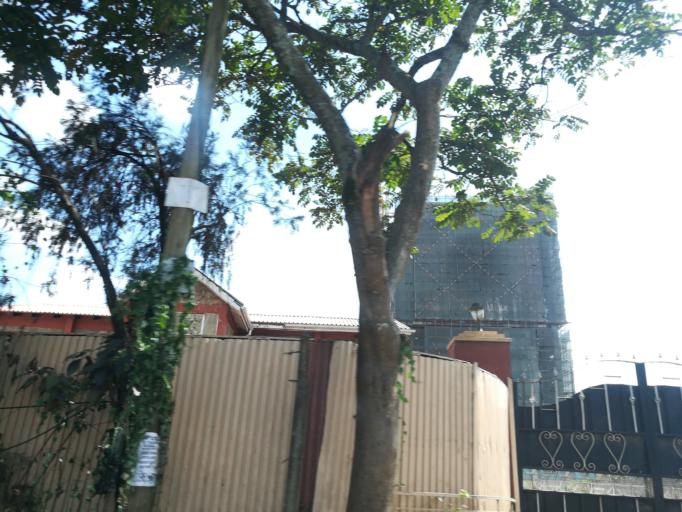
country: KE
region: Nairobi Area
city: Nairobi
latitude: -1.2979
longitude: 36.7885
